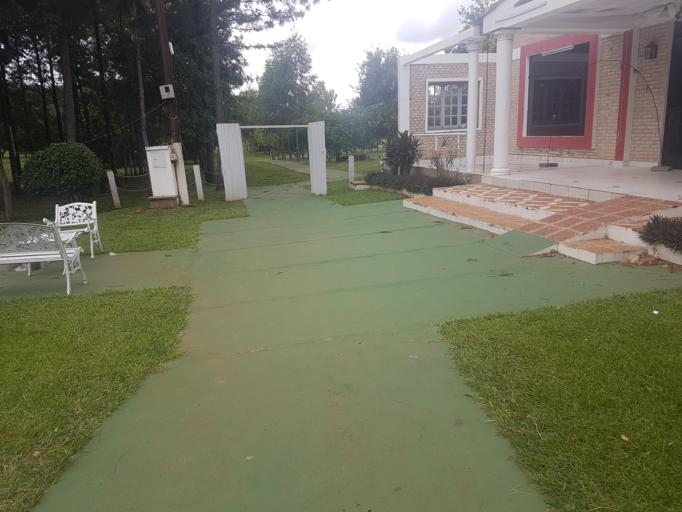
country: PY
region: Paraguari
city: Ybycui
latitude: -25.9990
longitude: -57.0505
